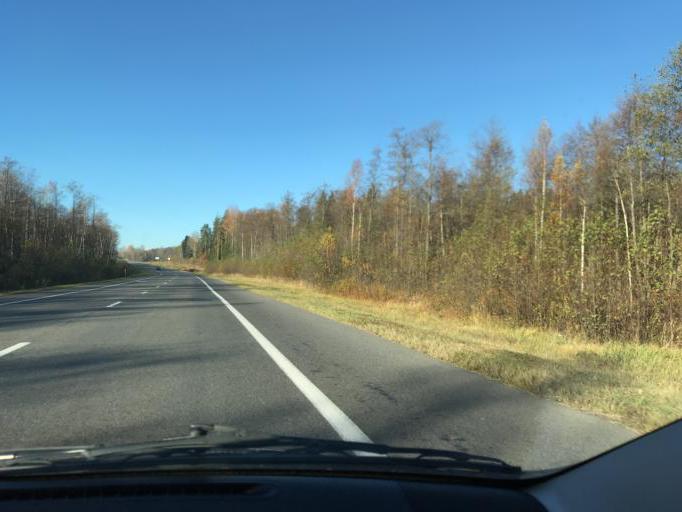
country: BY
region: Vitebsk
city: Vitebsk
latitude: 55.1033
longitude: 30.1793
